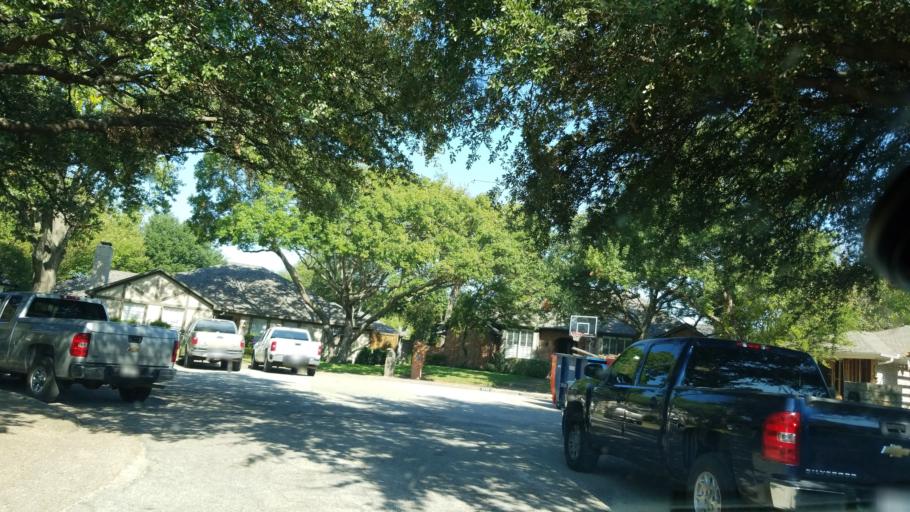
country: US
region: Texas
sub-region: Dallas County
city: Richardson
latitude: 32.9062
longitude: -96.7403
